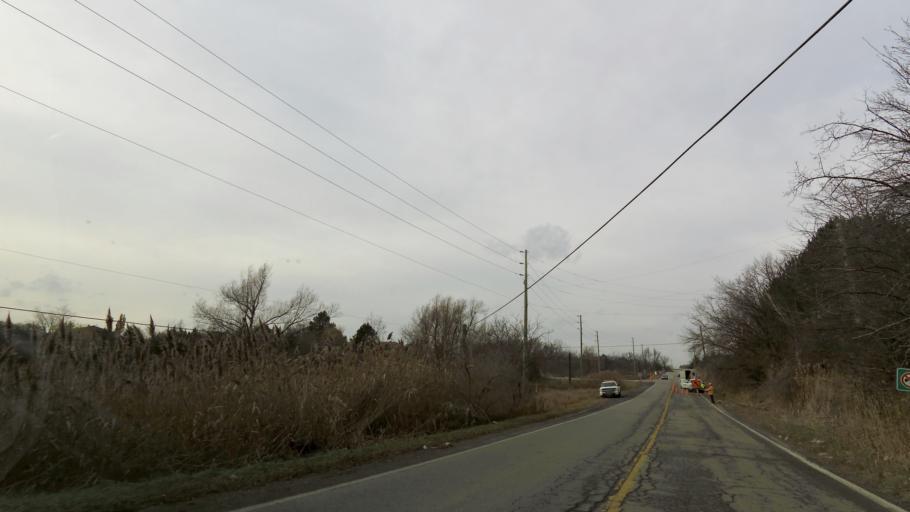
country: CA
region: Ontario
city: Etobicoke
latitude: 43.7604
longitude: -79.6473
